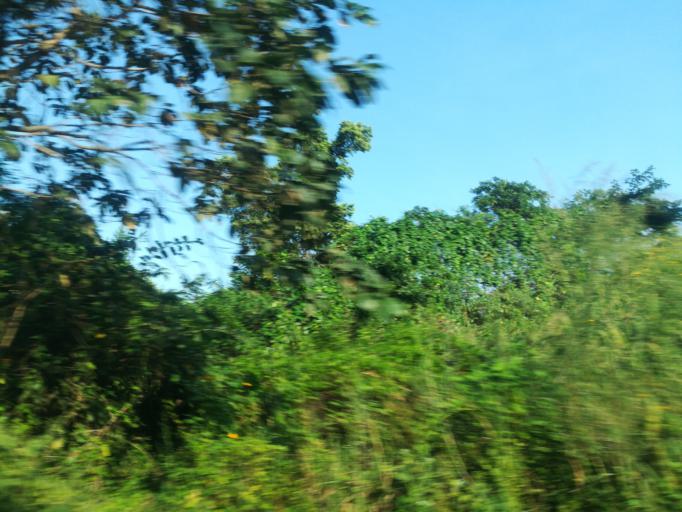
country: NG
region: Ogun
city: Abeokuta
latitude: 7.2556
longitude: 3.3003
